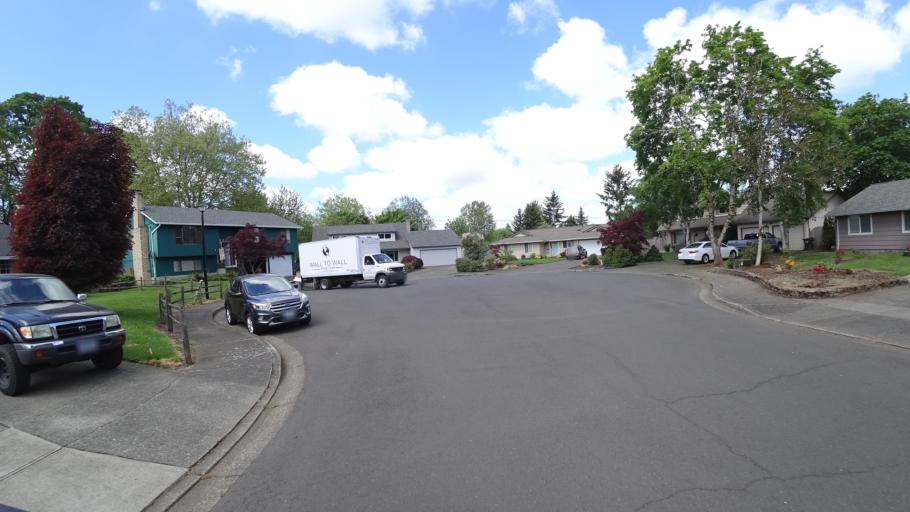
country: US
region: Oregon
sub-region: Washington County
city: Aloha
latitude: 45.5045
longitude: -122.8960
